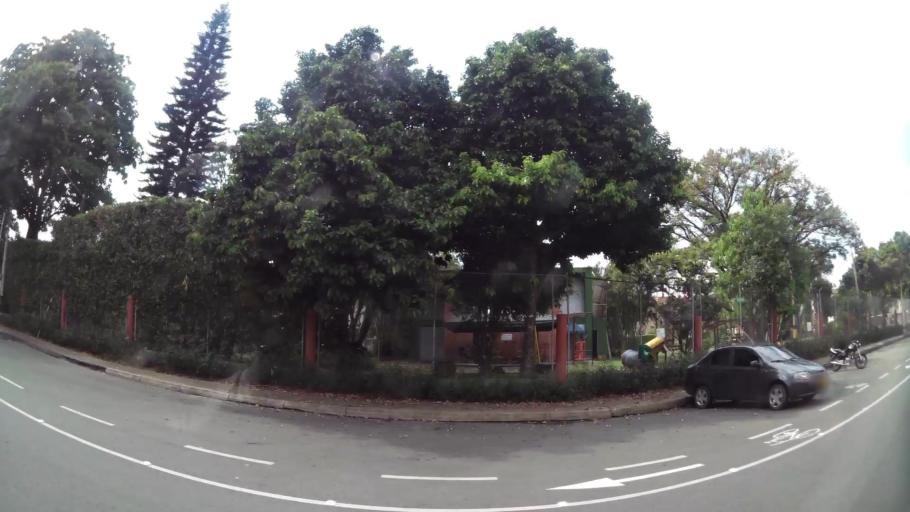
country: CO
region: Antioquia
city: Envigado
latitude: 6.1664
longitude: -75.5964
